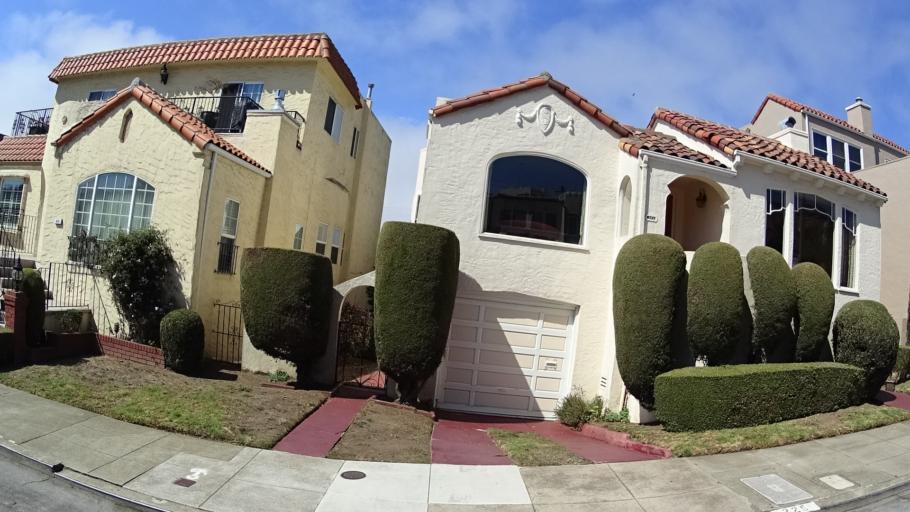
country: US
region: California
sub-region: San Mateo County
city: Daly City
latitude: 37.7304
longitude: -122.4645
